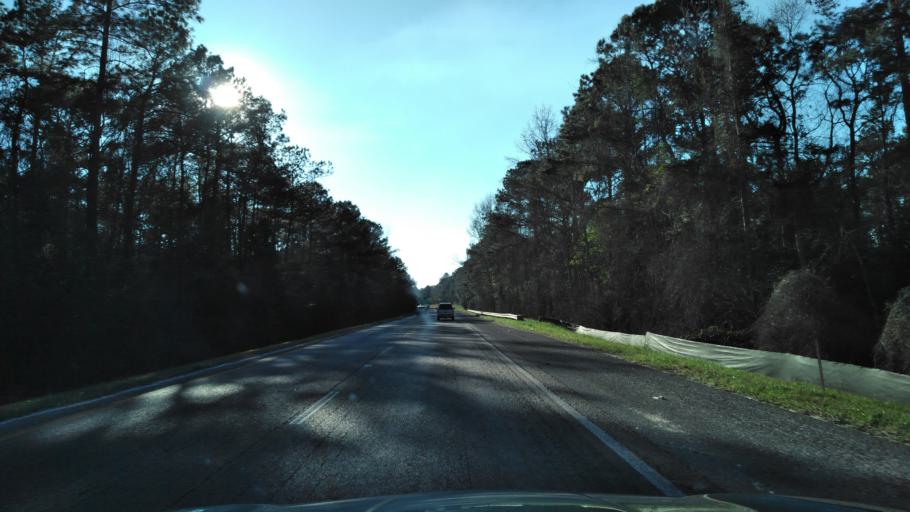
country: US
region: Alabama
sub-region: Baldwin County
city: Bay Minette
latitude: 30.9526
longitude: -87.8380
